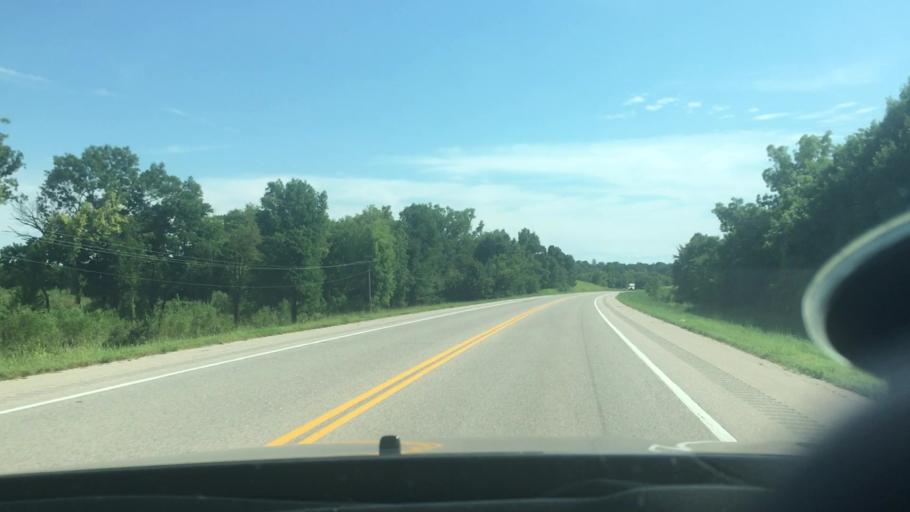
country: US
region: Oklahoma
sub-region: Seminole County
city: Konawa
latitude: 34.9553
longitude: -96.6787
